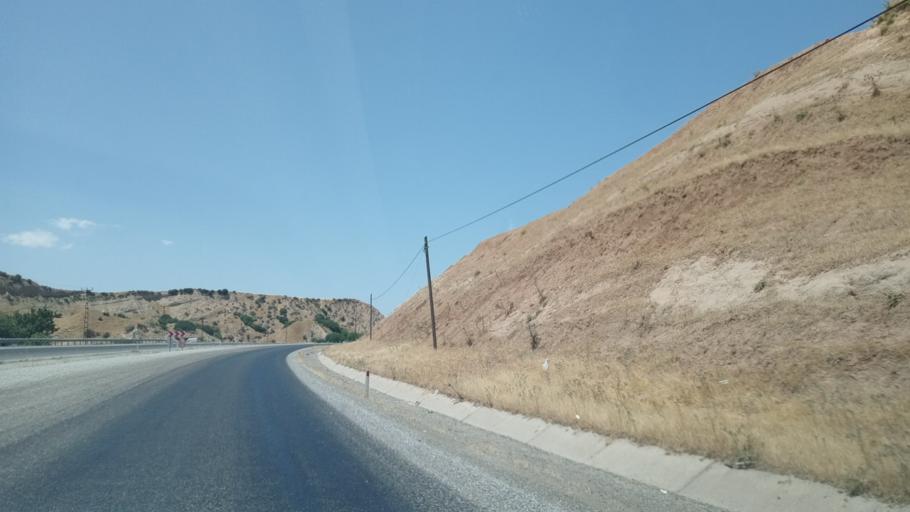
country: TR
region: Batman
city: Kozluk
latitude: 38.1695
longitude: 41.4581
